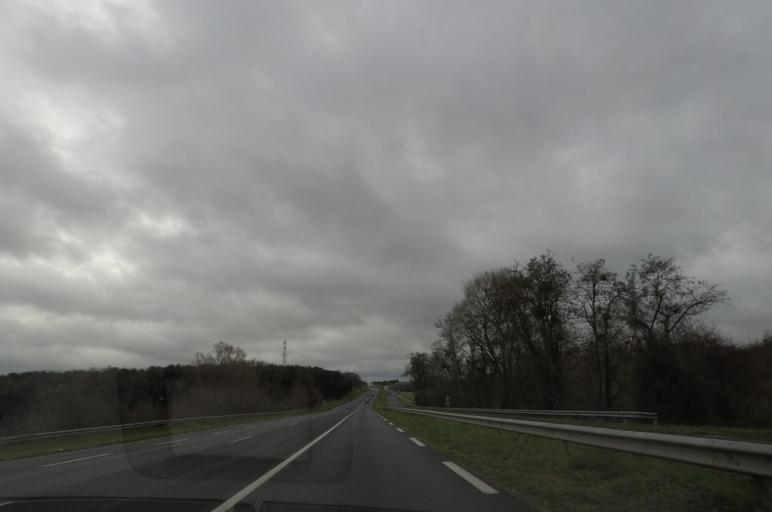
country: FR
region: Centre
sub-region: Departement du Loir-et-Cher
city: Saint-Sulpice-de-Pommeray
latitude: 47.6544
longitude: 1.2714
